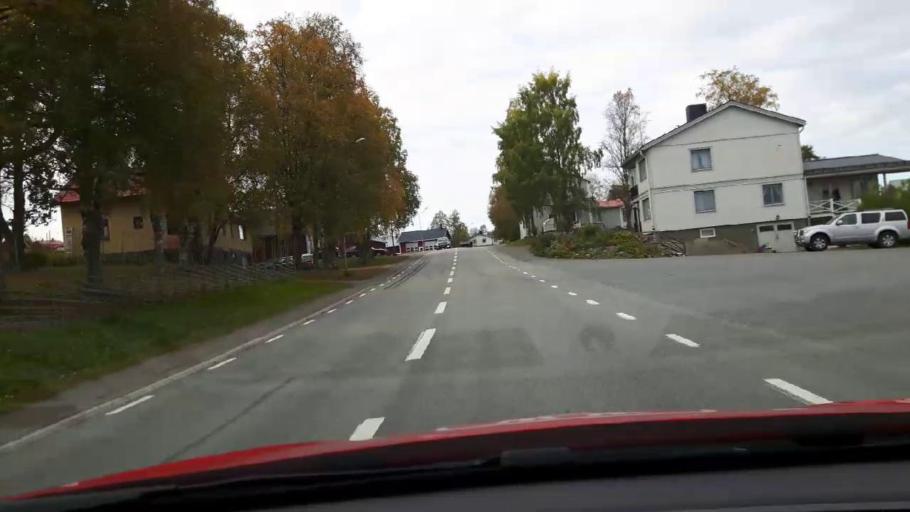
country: SE
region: Jaemtland
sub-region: Krokoms Kommun
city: Krokom
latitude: 63.1747
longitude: 14.0972
